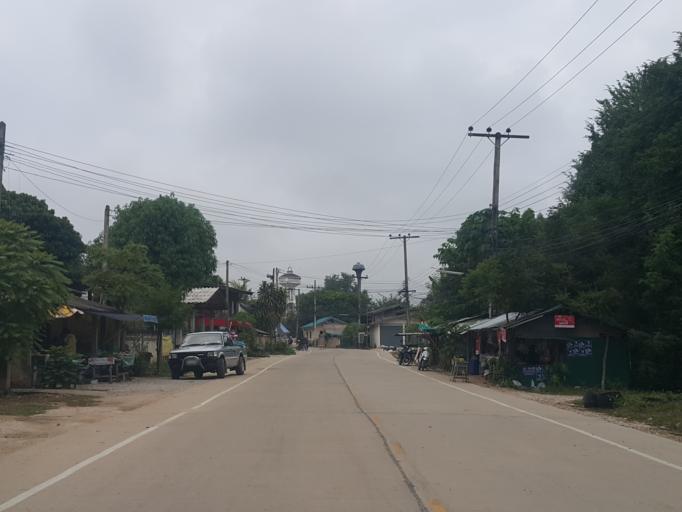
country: TH
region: Lampang
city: Lampang
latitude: 18.3184
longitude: 99.4913
